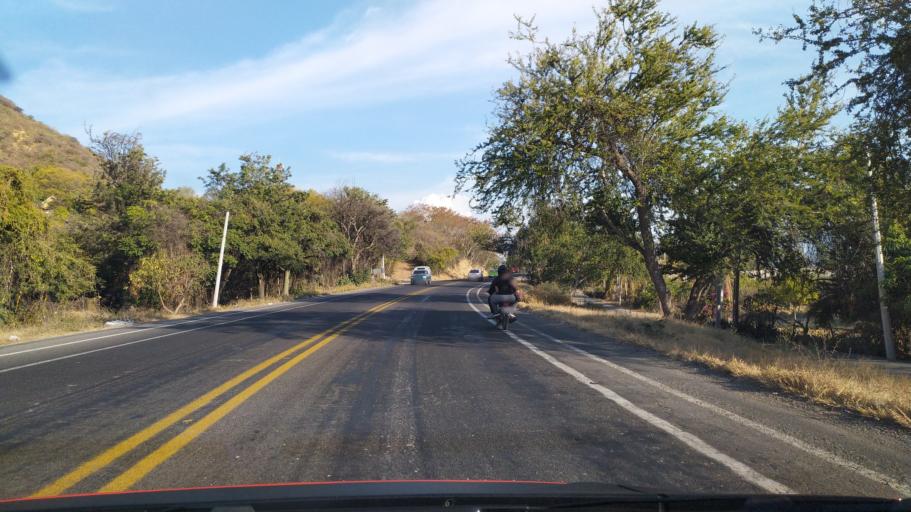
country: MX
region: Jalisco
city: Jamay
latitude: 20.2942
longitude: -102.7472
